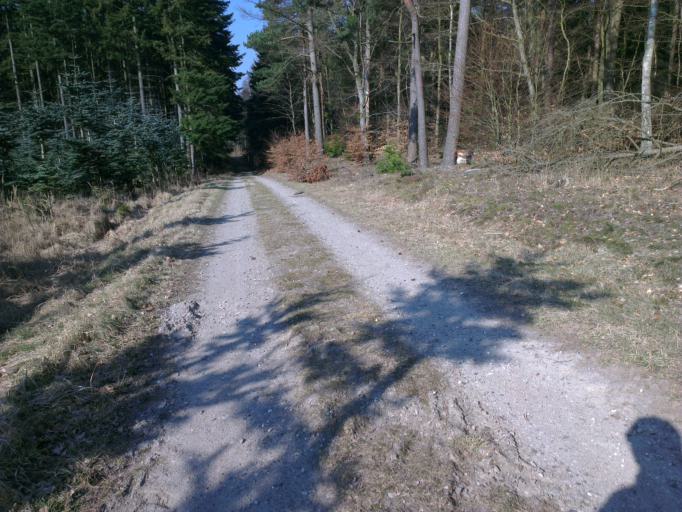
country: DK
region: Capital Region
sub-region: Frederikssund Kommune
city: Jaegerspris
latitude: 55.9030
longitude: 11.9901
